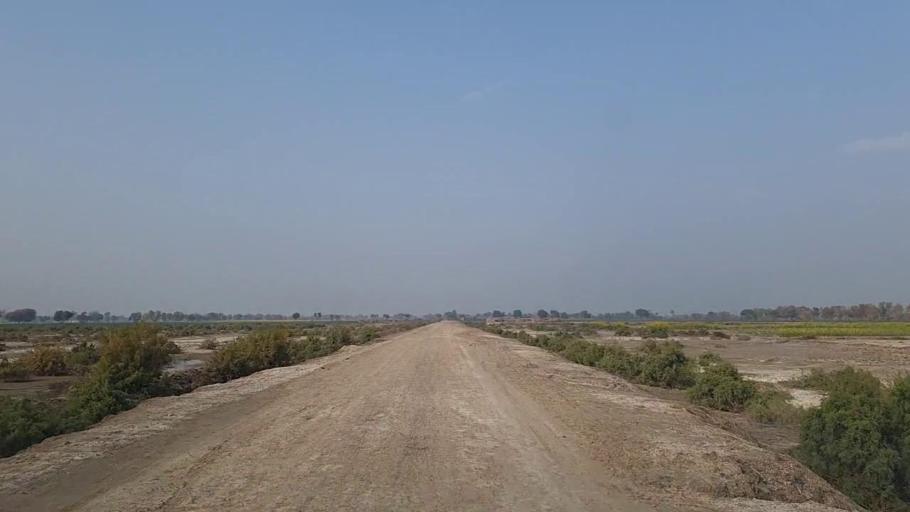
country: PK
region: Sindh
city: Nawabshah
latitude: 26.3436
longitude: 68.4738
